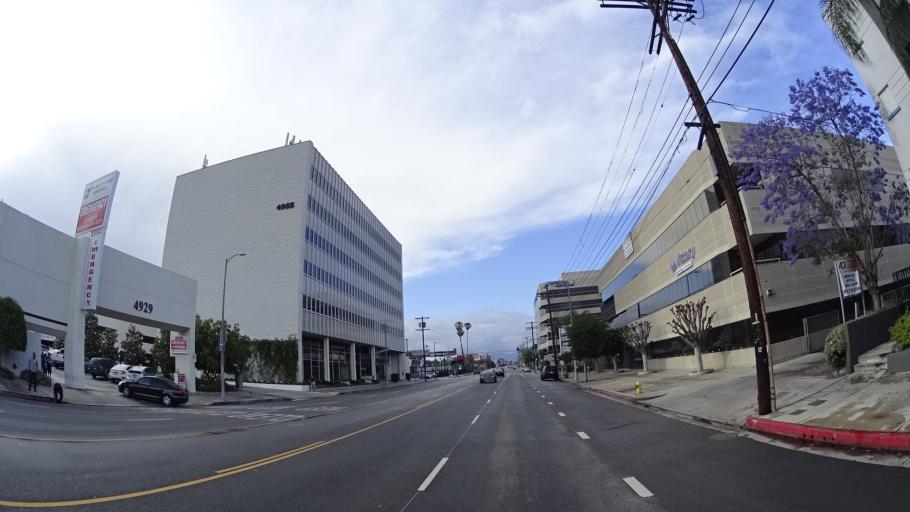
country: US
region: California
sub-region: Los Angeles County
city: Sherman Oaks
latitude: 34.1601
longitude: -118.4487
